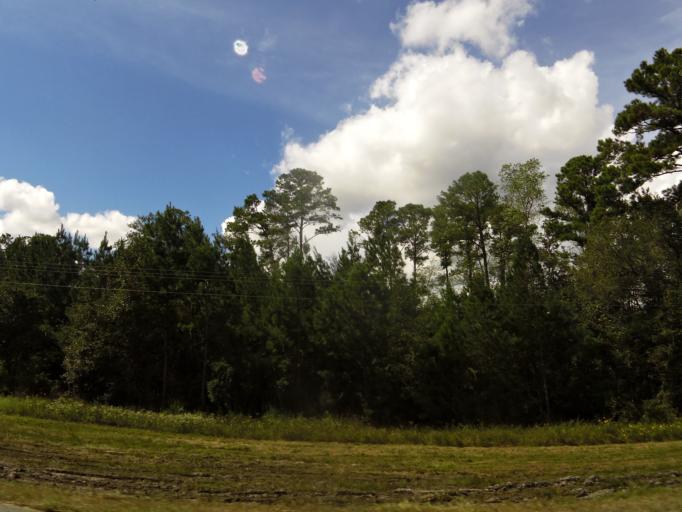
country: US
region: Georgia
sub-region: Brantley County
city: Nahunta
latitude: 31.0954
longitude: -82.0065
